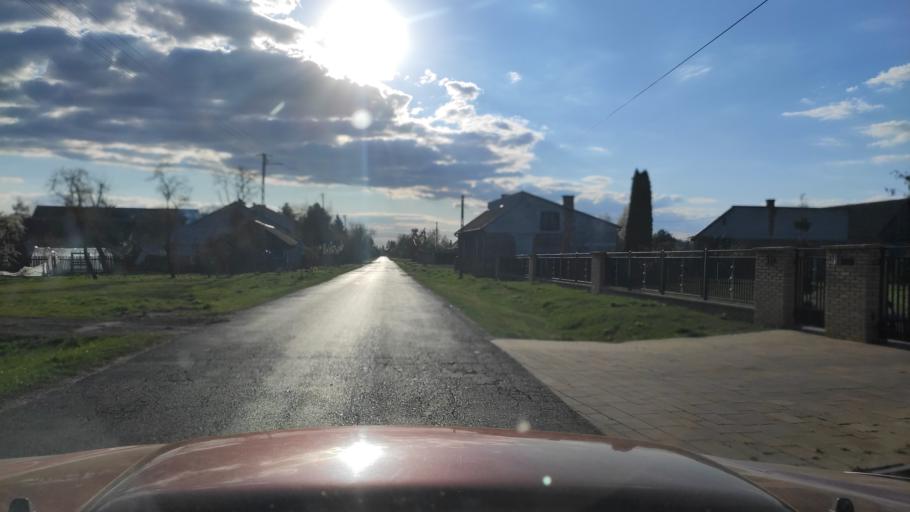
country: PL
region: Masovian Voivodeship
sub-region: Powiat zwolenski
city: Zwolen
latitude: 51.3843
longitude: 21.5749
